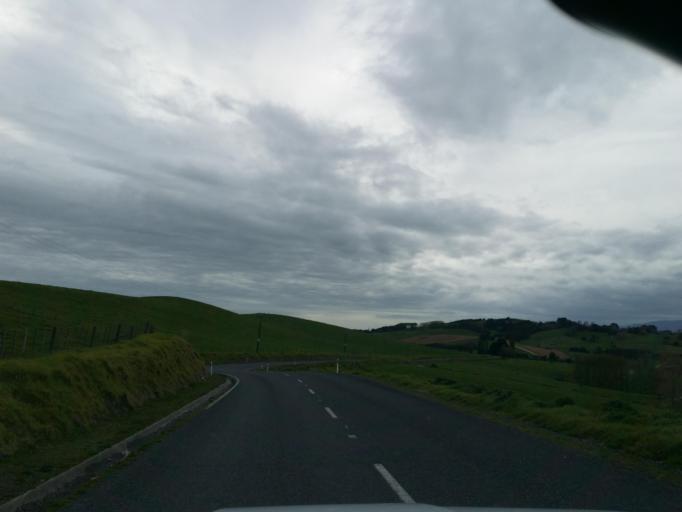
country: NZ
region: Northland
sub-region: Kaipara District
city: Dargaville
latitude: -35.9739
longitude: 173.9487
